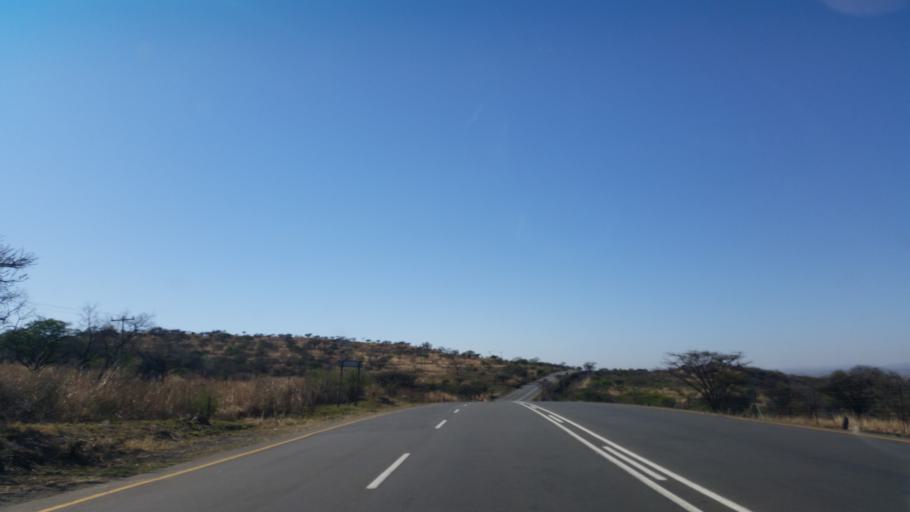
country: ZA
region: KwaZulu-Natal
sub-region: uThukela District Municipality
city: Ladysmith
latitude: -28.6914
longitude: 29.7601
